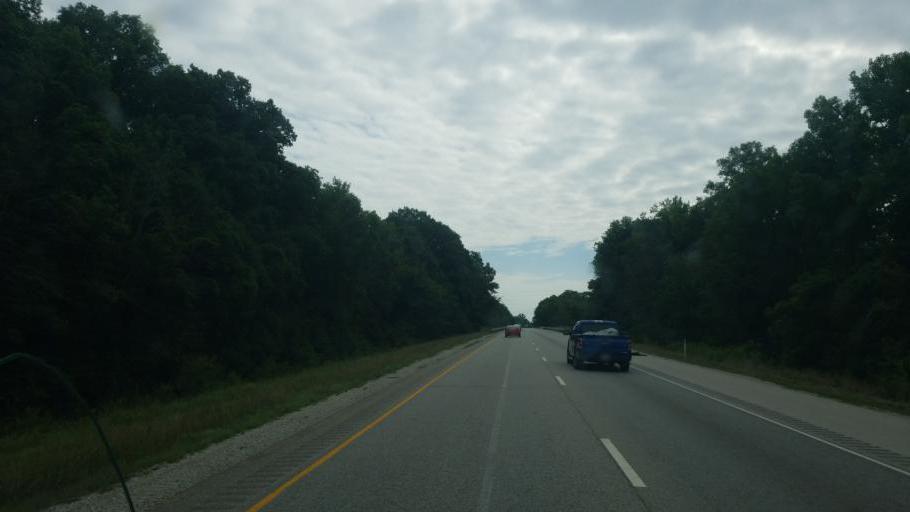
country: US
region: Indiana
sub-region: Vigo County
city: Seelyville
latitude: 39.4441
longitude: -87.2615
